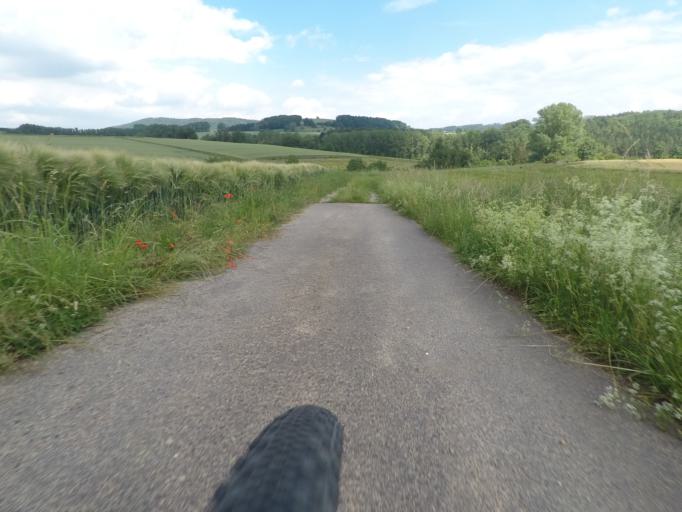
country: DE
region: Hesse
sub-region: Regierungsbezirk Kassel
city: Bad Sooden-Allendorf
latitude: 51.2491
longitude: 9.9116
